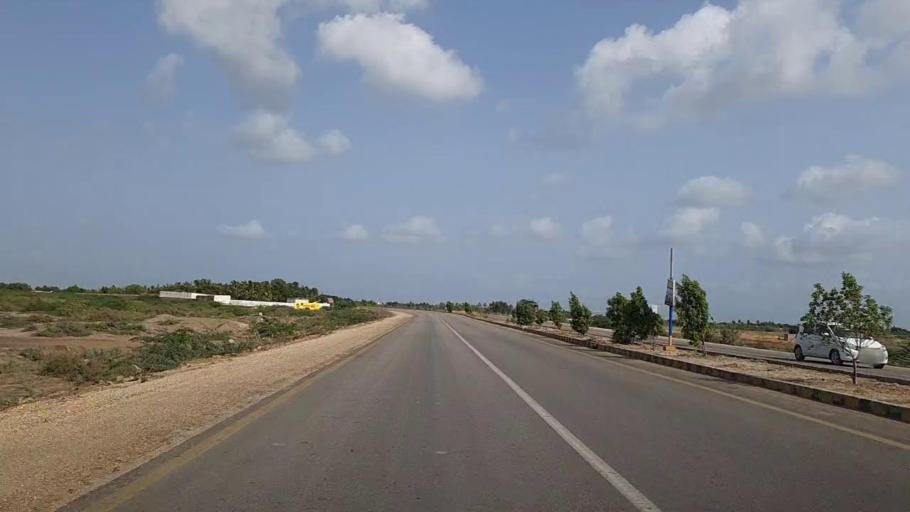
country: PK
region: Sindh
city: Gharo
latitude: 24.7323
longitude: 67.6032
